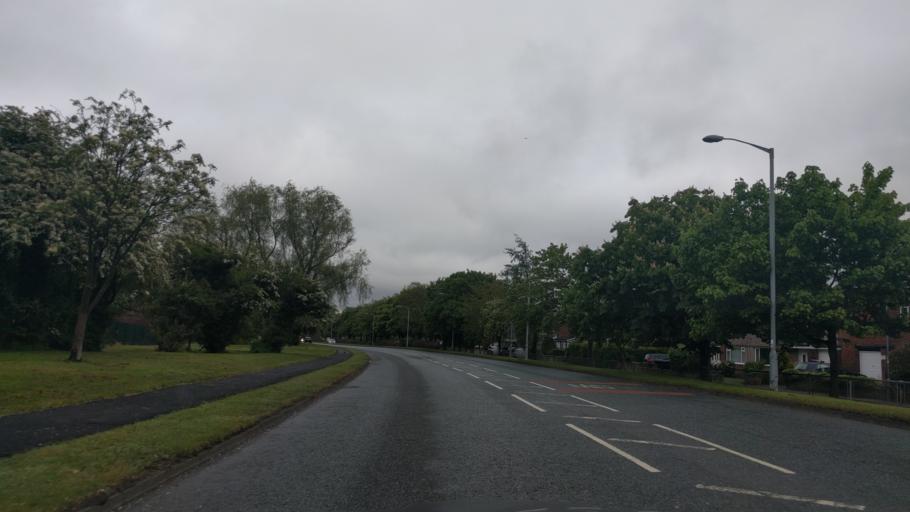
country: GB
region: England
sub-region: Northumberland
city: Morpeth
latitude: 55.1587
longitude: -1.6808
